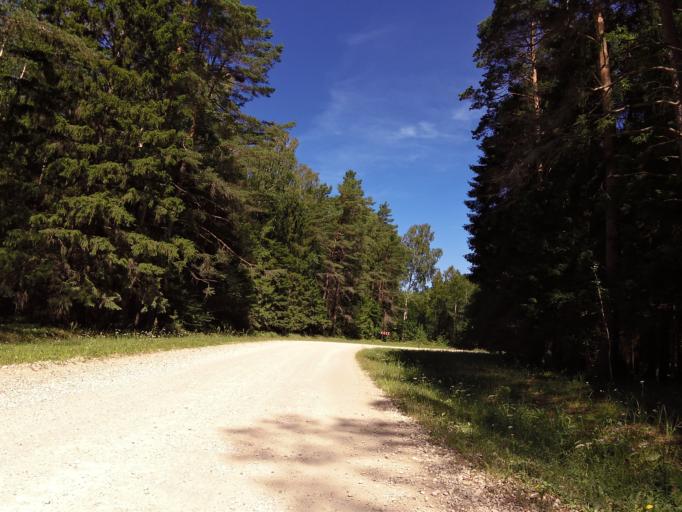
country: EE
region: Hiiumaa
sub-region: Kaerdla linn
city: Kardla
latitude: 58.9196
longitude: 22.3507
